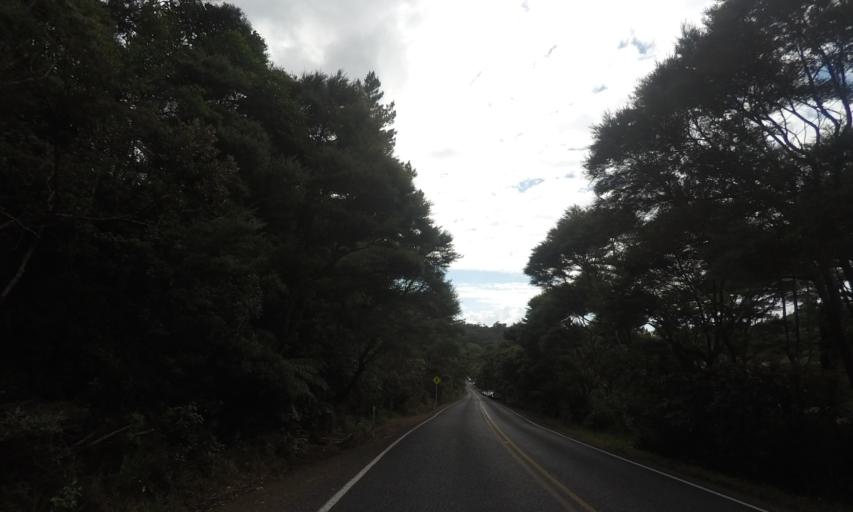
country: NZ
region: Auckland
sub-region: Auckland
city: Titirangi
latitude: -36.9999
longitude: 174.5881
